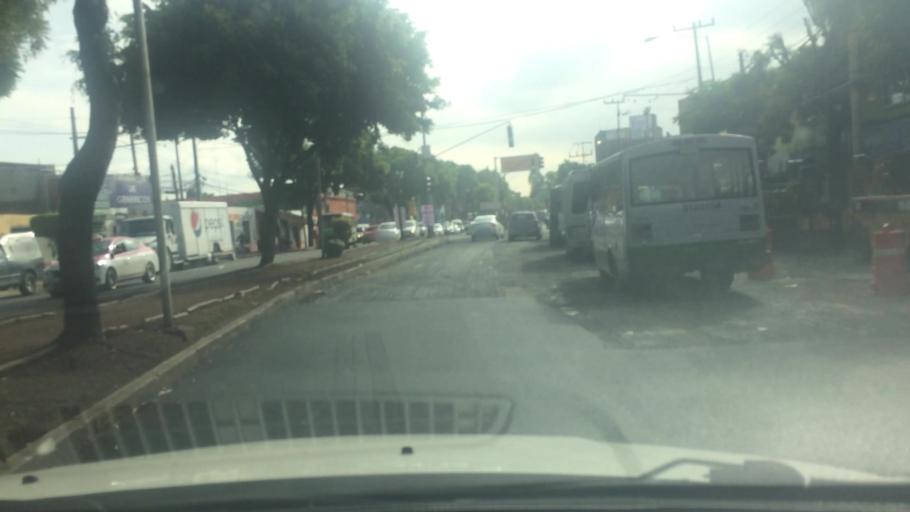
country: MX
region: Mexico City
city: Coyoacan
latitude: 19.3381
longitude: -99.1187
